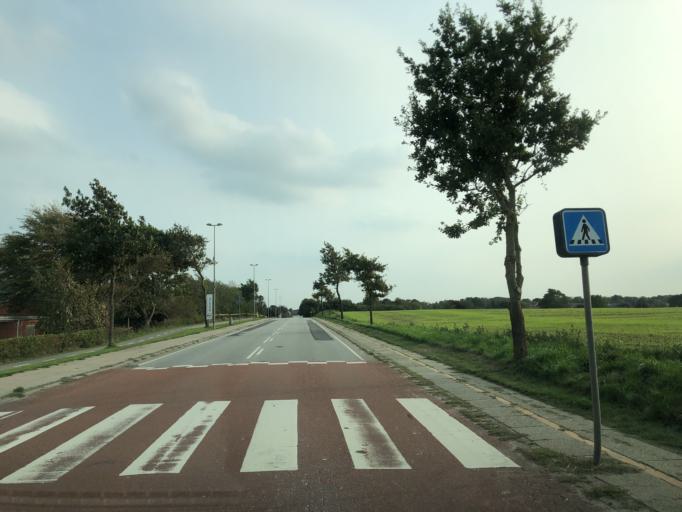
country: DK
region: Central Jutland
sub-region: Ringkobing-Skjern Kommune
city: Videbaek
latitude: 56.0911
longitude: 8.7025
